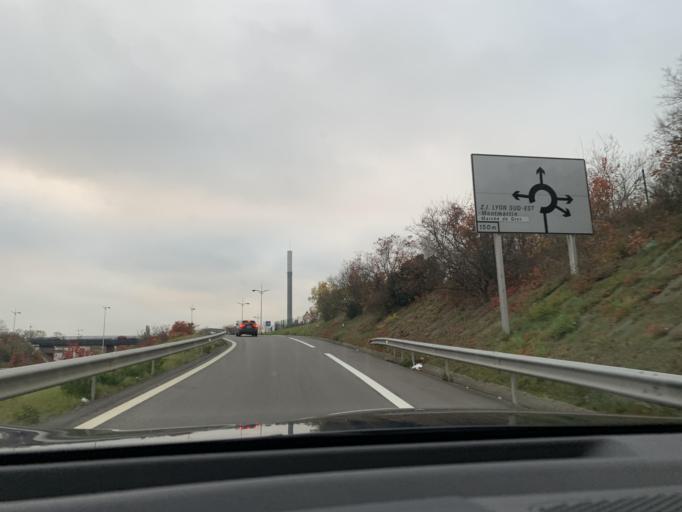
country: FR
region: Rhone-Alpes
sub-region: Departement du Rhone
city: Corbas
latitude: 45.6713
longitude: 4.9116
